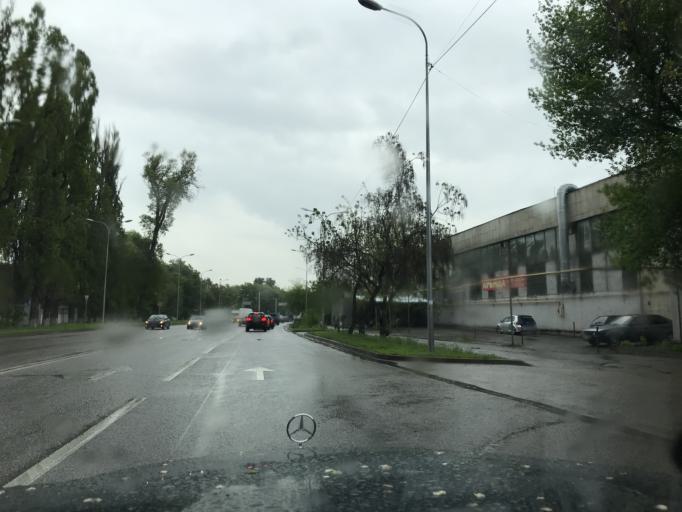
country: KZ
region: Almaty Oblysy
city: Pervomayskiy
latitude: 43.3448
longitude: 76.9679
